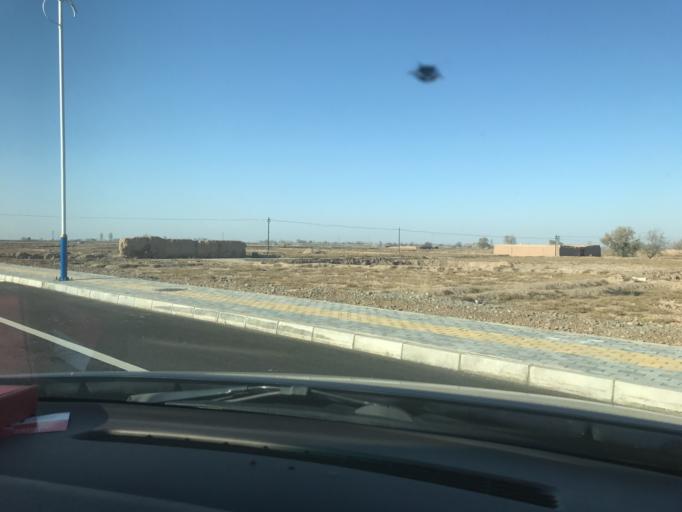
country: CN
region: Gansu Sheng
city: Gulang
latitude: 37.6249
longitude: 103.0025
